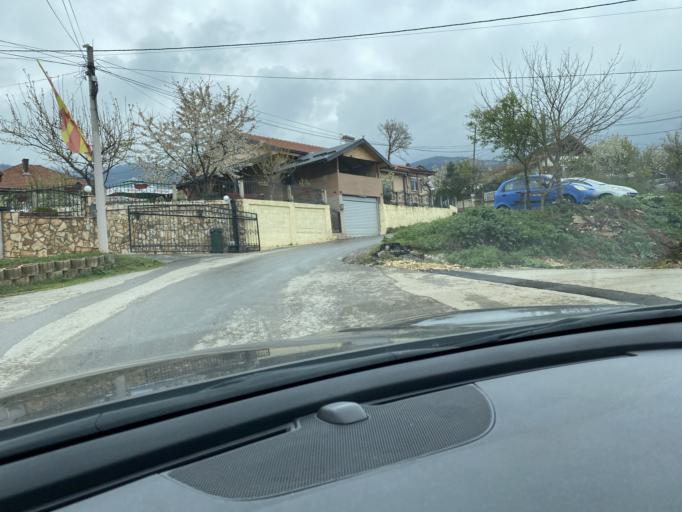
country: MK
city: Creshevo
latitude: 42.0517
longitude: 21.5187
